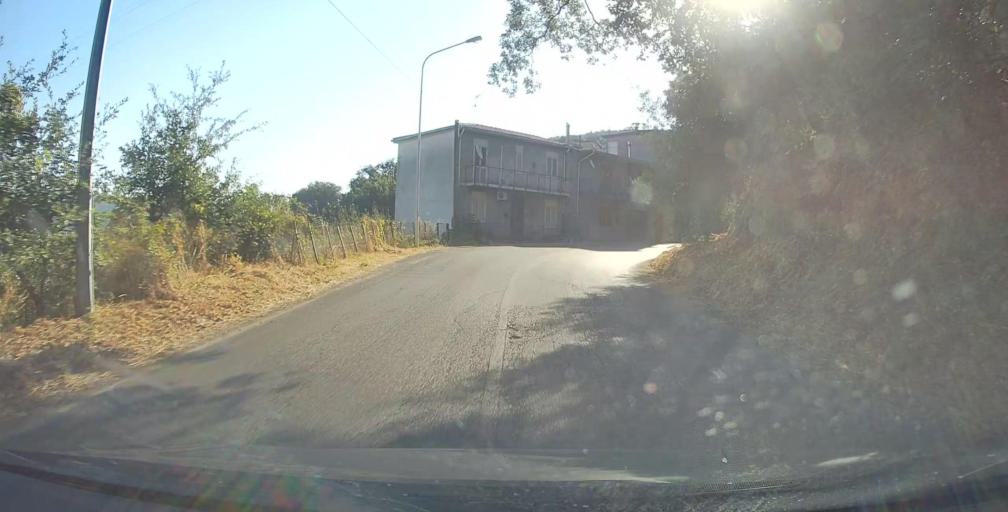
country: IT
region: Sicily
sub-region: Messina
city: San Piero Patti
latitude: 38.0766
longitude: 14.9778
